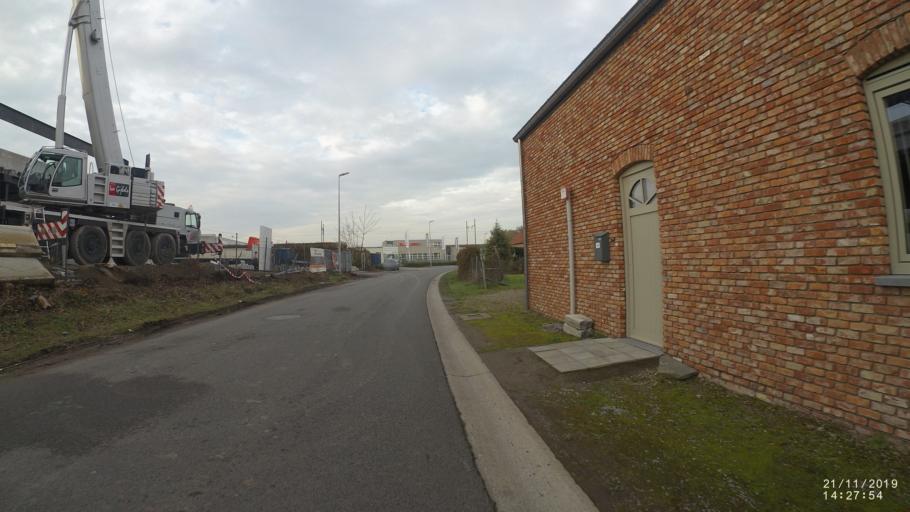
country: BE
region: Flanders
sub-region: Provincie Limburg
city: Alken
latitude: 50.8921
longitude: 5.3050
